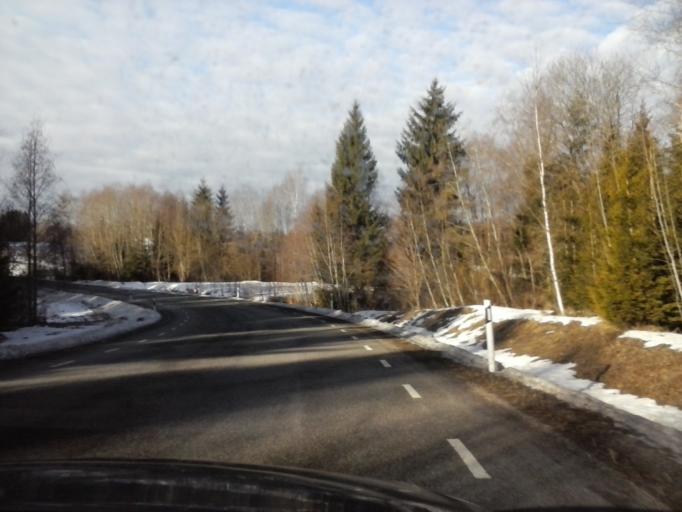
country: EE
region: Tartu
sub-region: Elva linn
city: Elva
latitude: 58.0468
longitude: 26.4021
